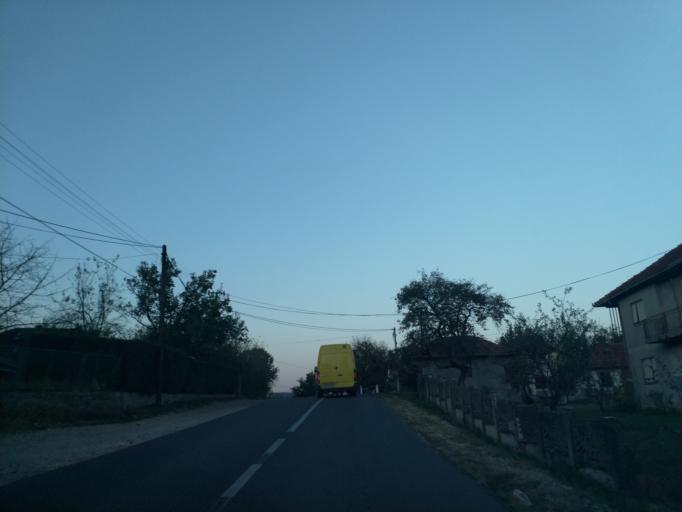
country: RS
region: Central Serbia
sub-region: Rasinski Okrug
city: Krusevac
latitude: 43.6072
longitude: 21.2873
